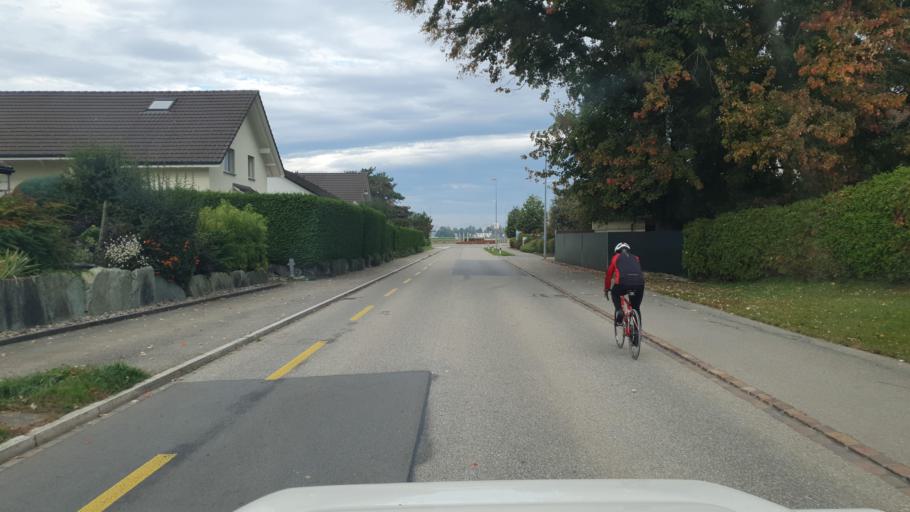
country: CH
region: Aargau
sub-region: Bezirk Muri
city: Waltenschwil
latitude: 47.3369
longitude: 8.2972
